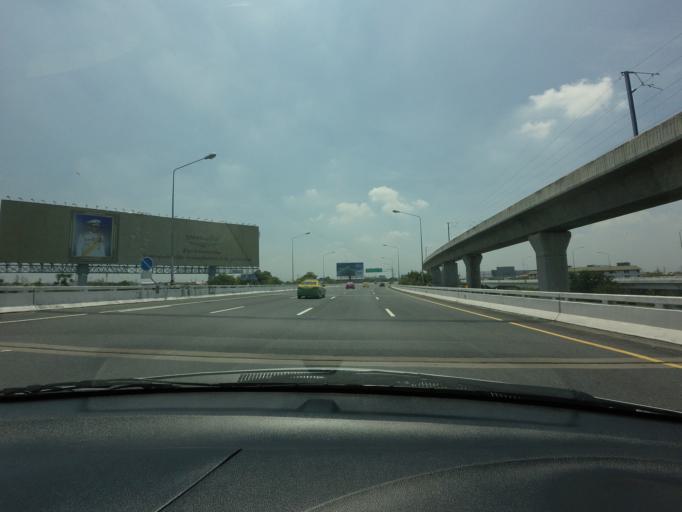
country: TH
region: Bangkok
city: Lat Krabang
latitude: 13.7252
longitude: 100.7605
